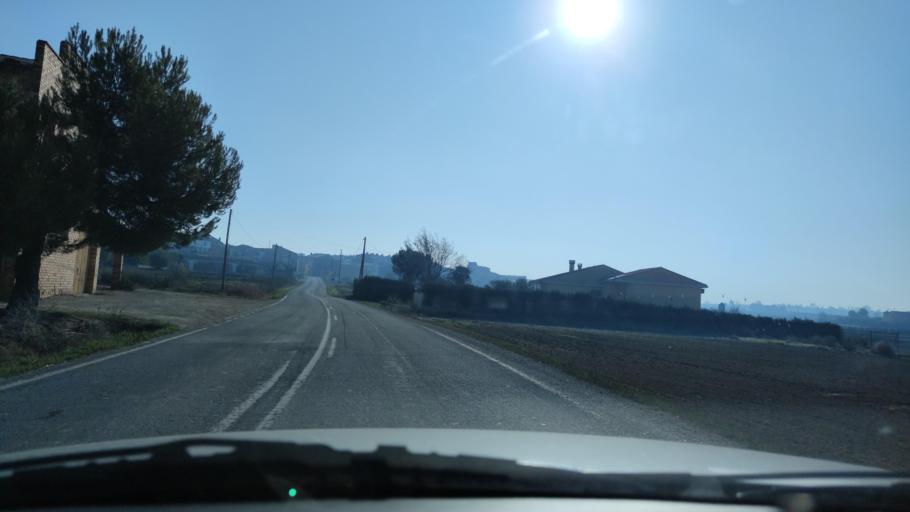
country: ES
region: Catalonia
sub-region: Provincia de Lleida
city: Alcoletge
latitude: 41.6184
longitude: 0.7340
